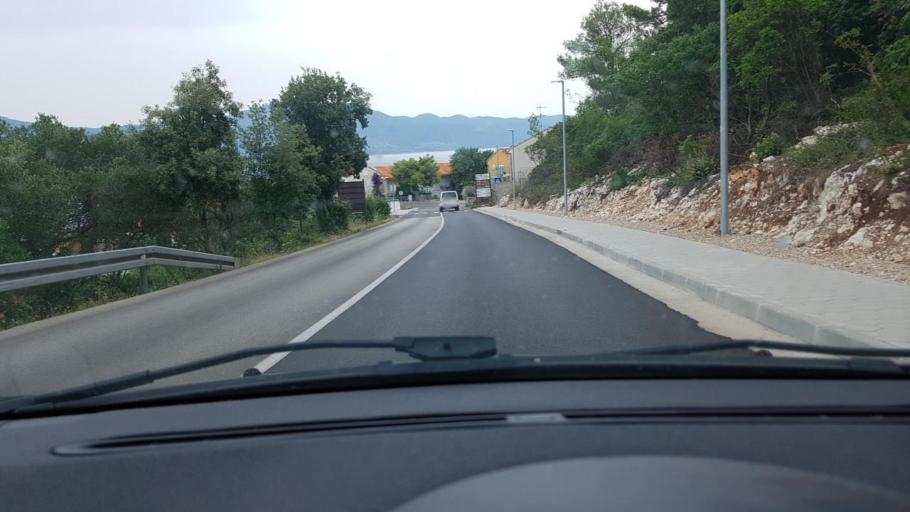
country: HR
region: Dubrovacko-Neretvanska
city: Korcula
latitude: 42.9568
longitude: 17.1336
